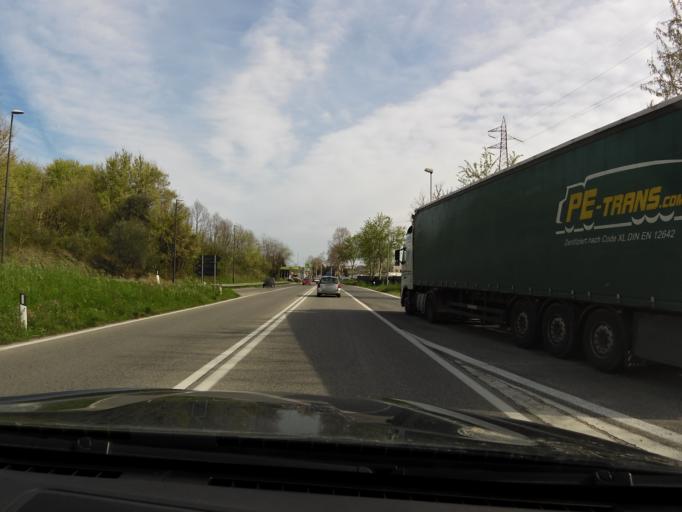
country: IT
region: The Marches
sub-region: Provincia di Macerata
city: Porto Recanati
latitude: 43.4378
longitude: 13.6414
